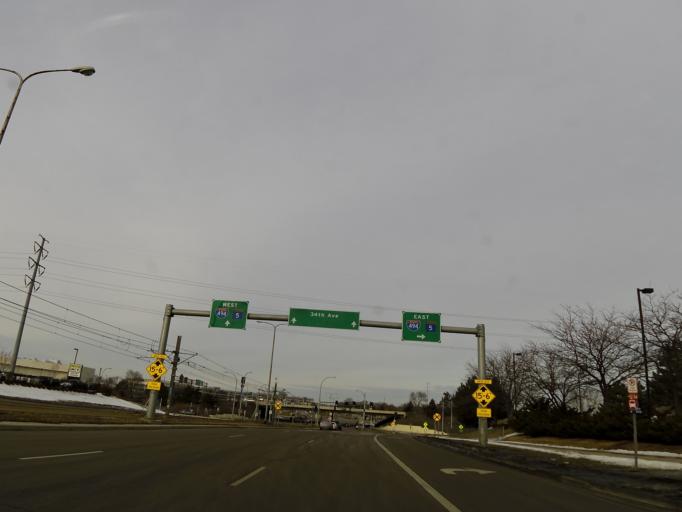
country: US
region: Minnesota
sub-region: Hennepin County
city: Richfield
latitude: 44.8601
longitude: -93.2229
